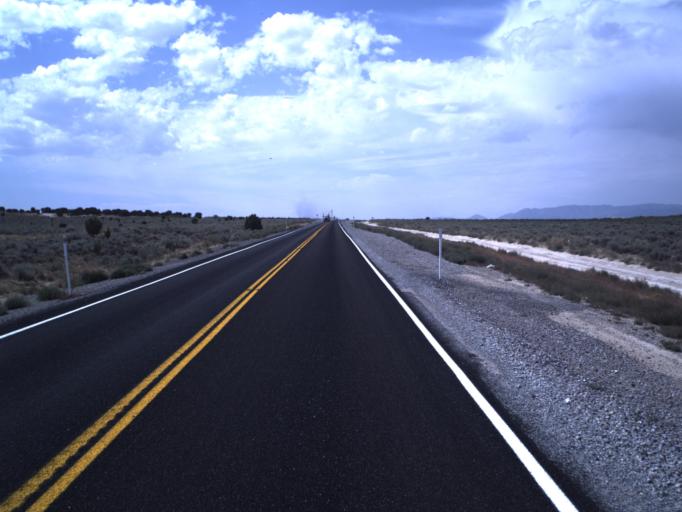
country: US
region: Utah
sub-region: Utah County
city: Eagle Mountain
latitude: 40.2339
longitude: -112.1707
